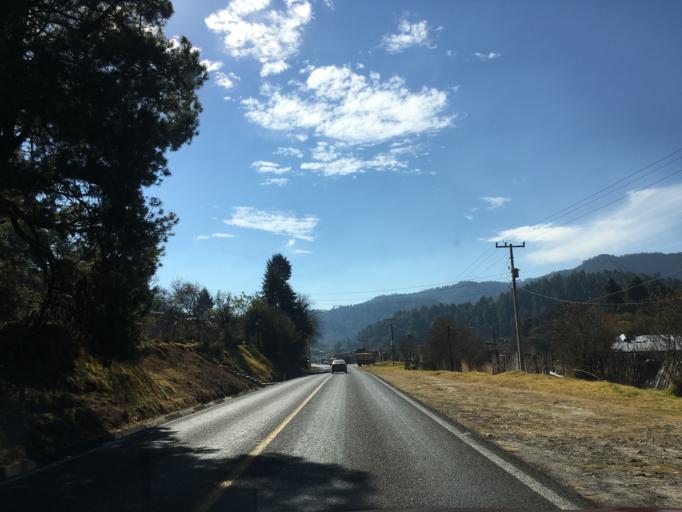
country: MX
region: Michoacan
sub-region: Hidalgo
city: Tierras Coloradas (San Pedro)
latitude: 19.6863
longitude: -100.7419
